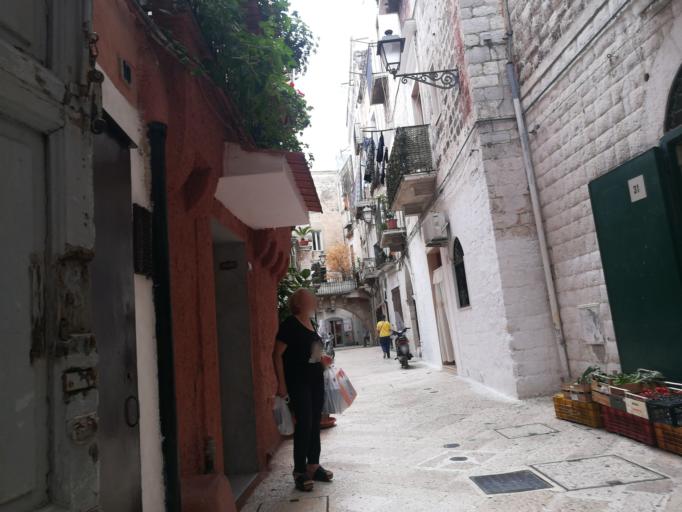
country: IT
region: Apulia
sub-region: Provincia di Bari
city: Bari
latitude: 41.1289
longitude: 16.8695
